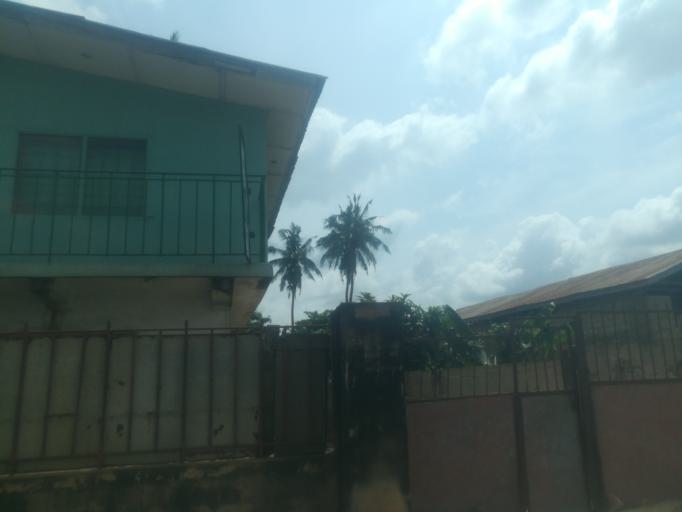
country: NG
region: Oyo
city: Ibadan
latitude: 7.3582
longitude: 3.8805
